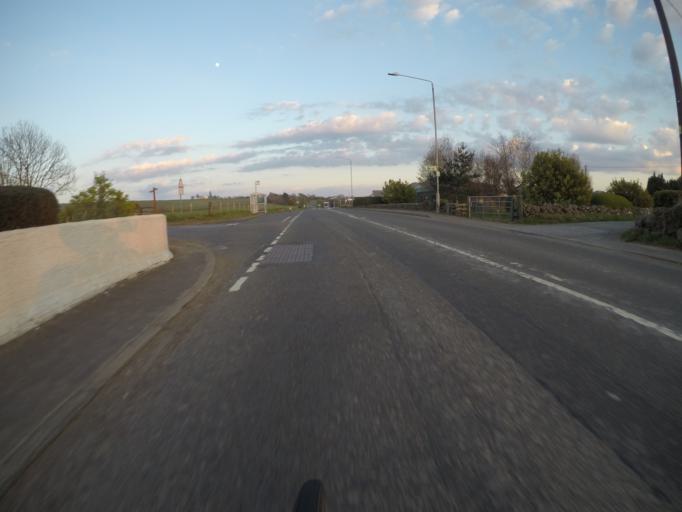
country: GB
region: Scotland
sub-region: South Ayrshire
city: Troon
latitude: 55.5593
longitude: -4.6300
